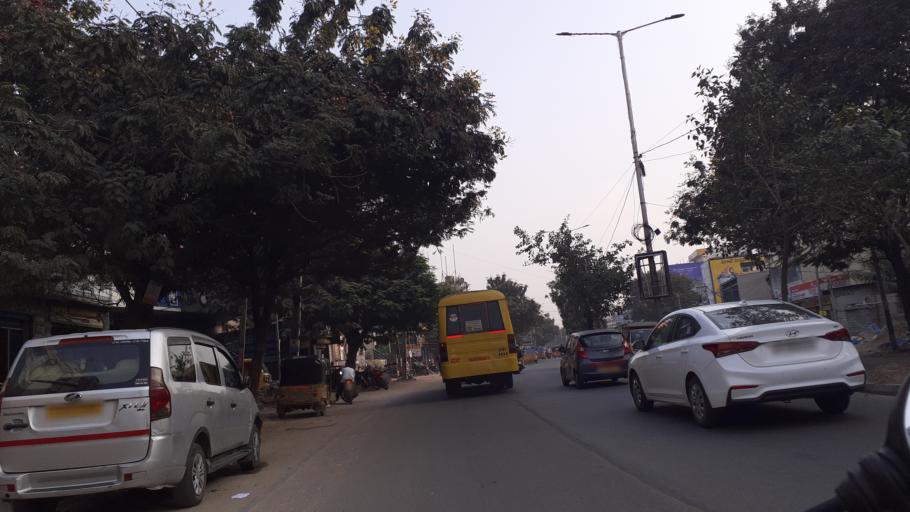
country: IN
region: Telangana
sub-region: Rangareddi
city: Kukatpalli
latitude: 17.4771
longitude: 78.3628
